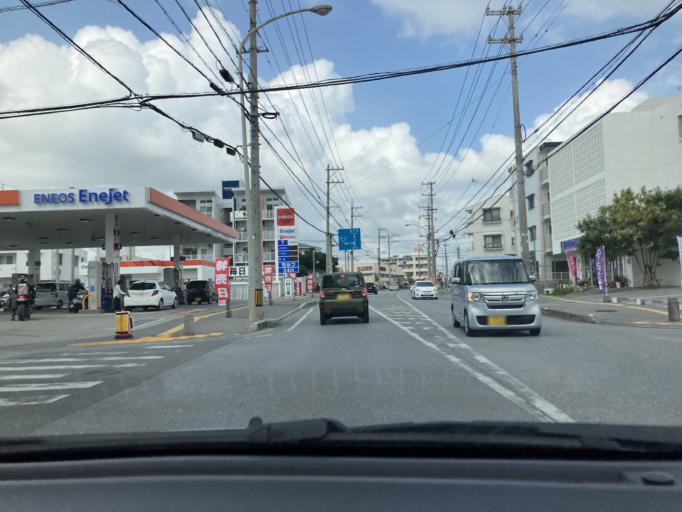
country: JP
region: Okinawa
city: Ginowan
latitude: 26.2516
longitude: 127.7722
